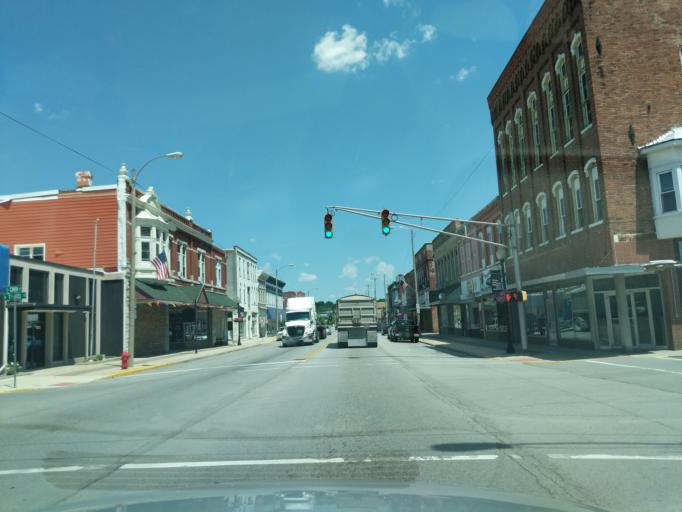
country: US
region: Indiana
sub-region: Noble County
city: Ligonier
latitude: 41.4637
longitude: -85.5876
